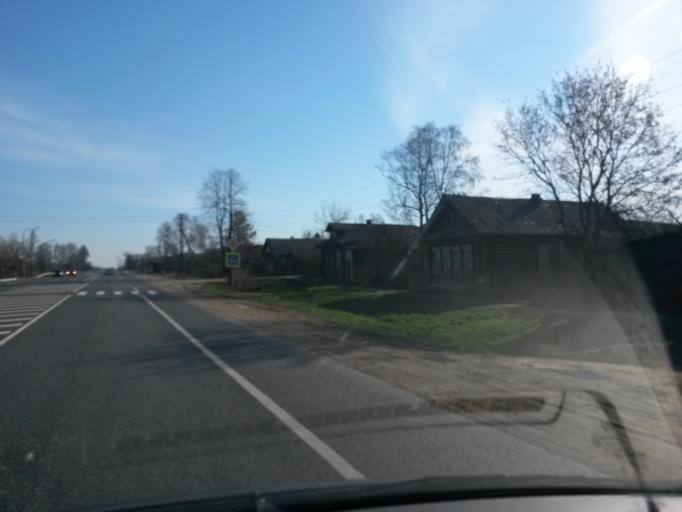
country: RU
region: Jaroslavl
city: Petrovsk
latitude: 56.9331
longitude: 39.1544
